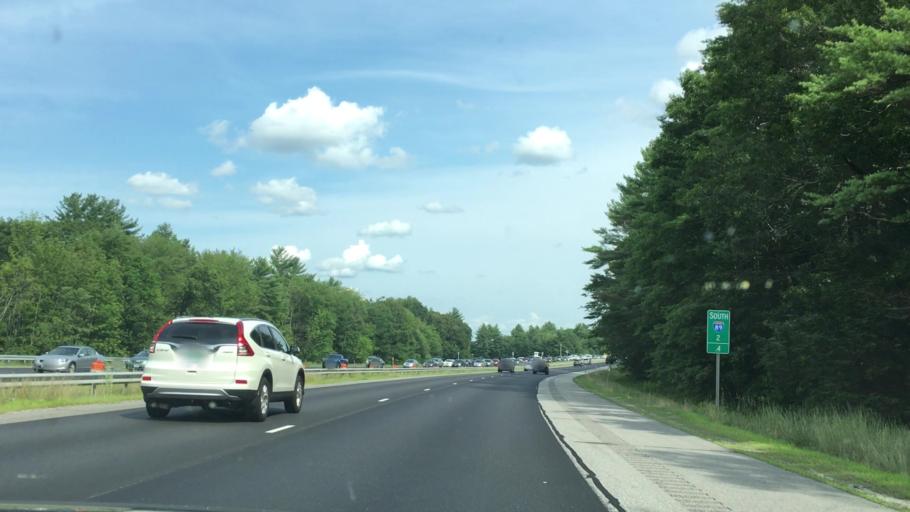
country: US
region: New Hampshire
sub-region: Merrimack County
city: Concord
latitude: 43.1822
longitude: -71.5722
